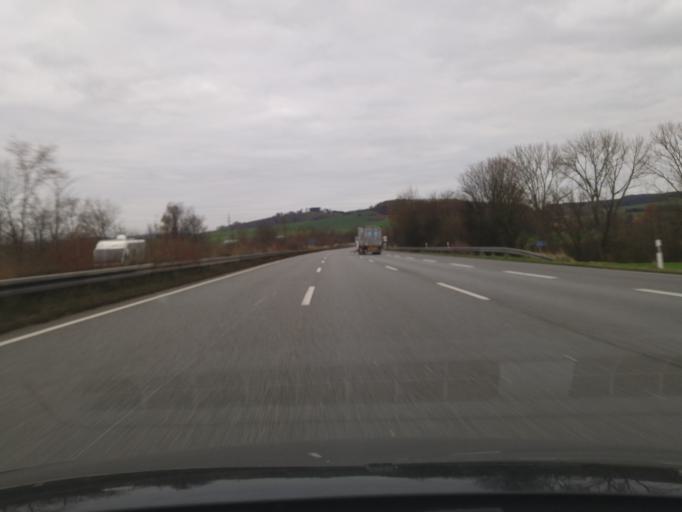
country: DE
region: Lower Saxony
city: Hillerse
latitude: 51.7015
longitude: 9.9380
